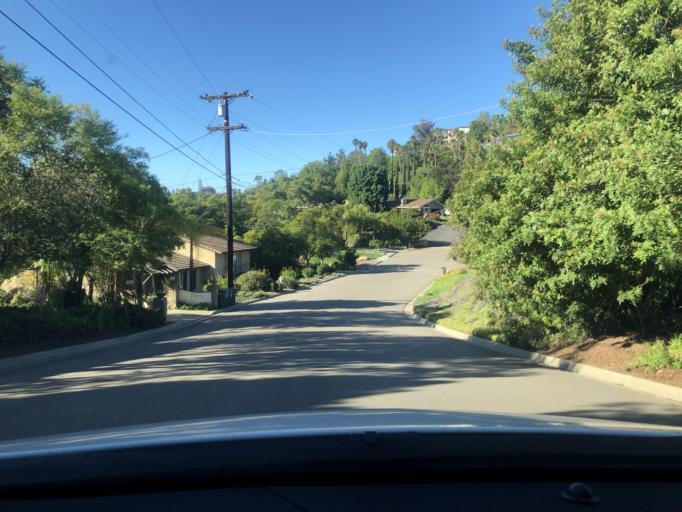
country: US
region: California
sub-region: San Diego County
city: Rancho San Diego
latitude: 32.7665
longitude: -116.9433
